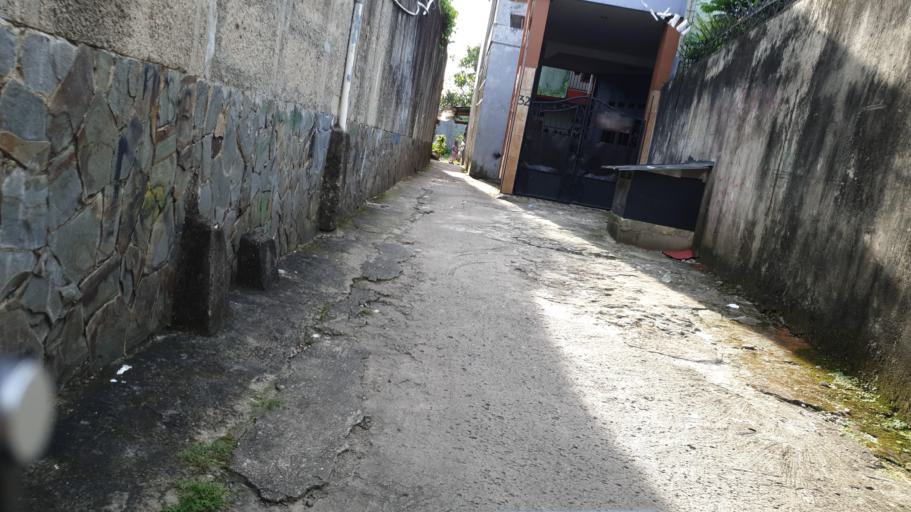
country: ID
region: Banten
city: South Tangerang
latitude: -6.2905
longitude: 106.7893
